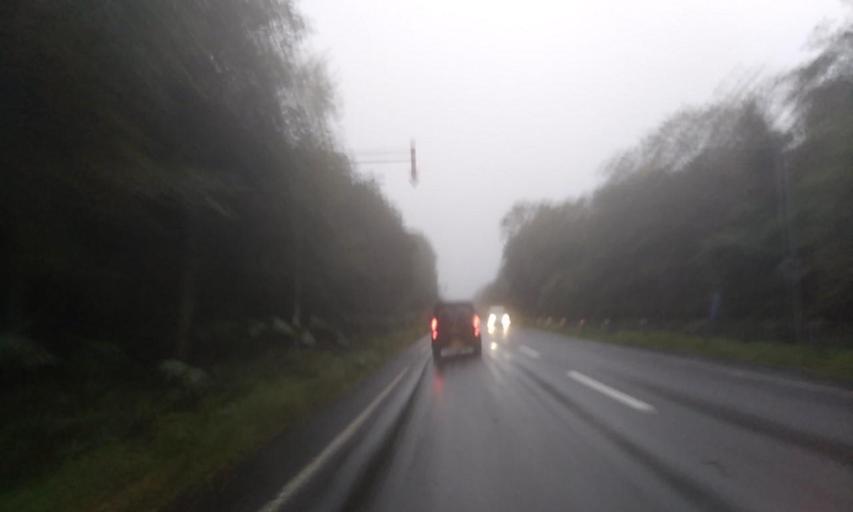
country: JP
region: Hokkaido
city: Kushiro
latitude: 42.9816
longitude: 144.5472
